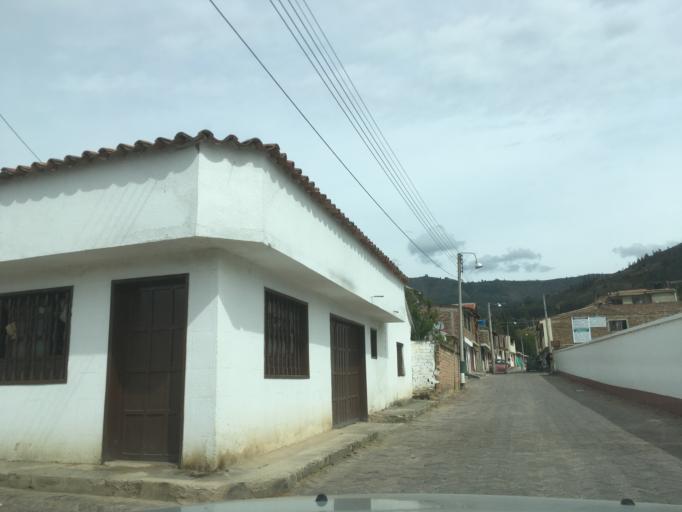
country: CO
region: Boyaca
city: Firavitoba
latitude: 5.6108
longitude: -72.9794
